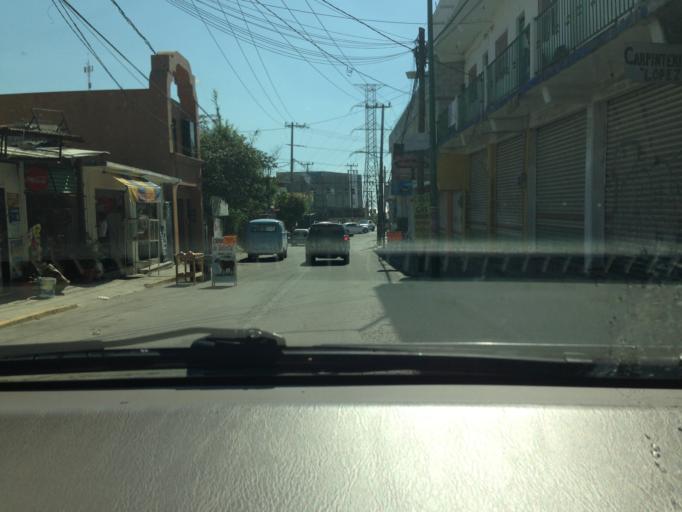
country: MX
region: Morelos
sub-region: Cuernavaca
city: Fraccionamiento Lomas de Ahuatlan
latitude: 18.9647
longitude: -99.2278
